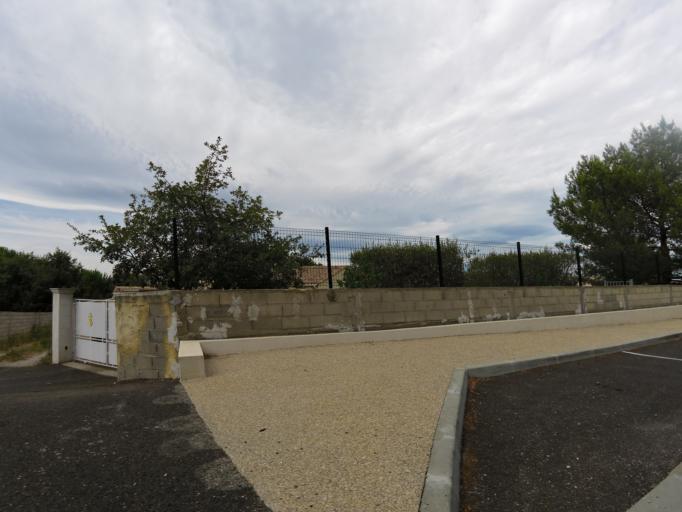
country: FR
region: Languedoc-Roussillon
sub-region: Departement du Gard
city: Saint-Genies-de-Malgoires
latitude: 43.9324
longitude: 4.2370
